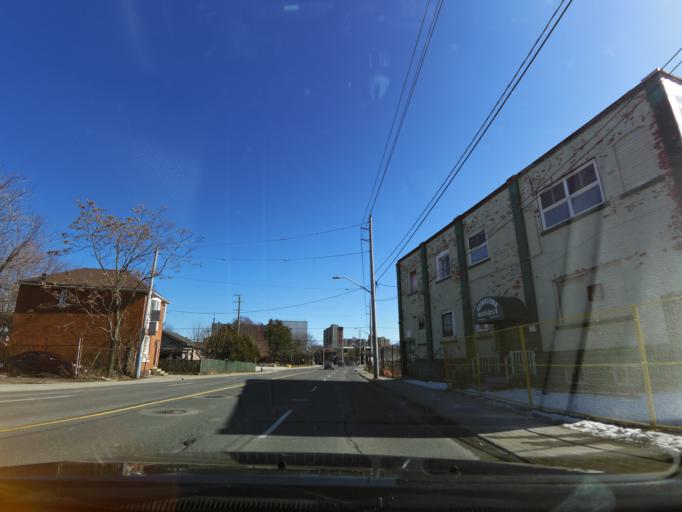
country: CA
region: Ontario
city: Hamilton
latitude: 43.2581
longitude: -79.8638
